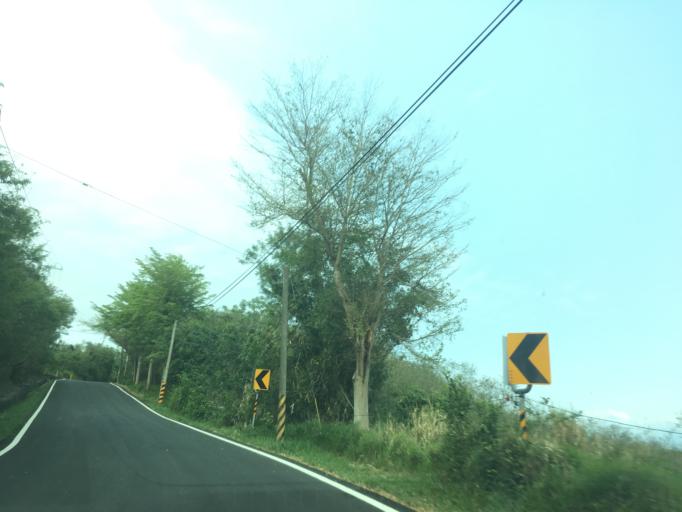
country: TW
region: Taiwan
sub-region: Taitung
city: Taitung
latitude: 22.7886
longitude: 121.1605
